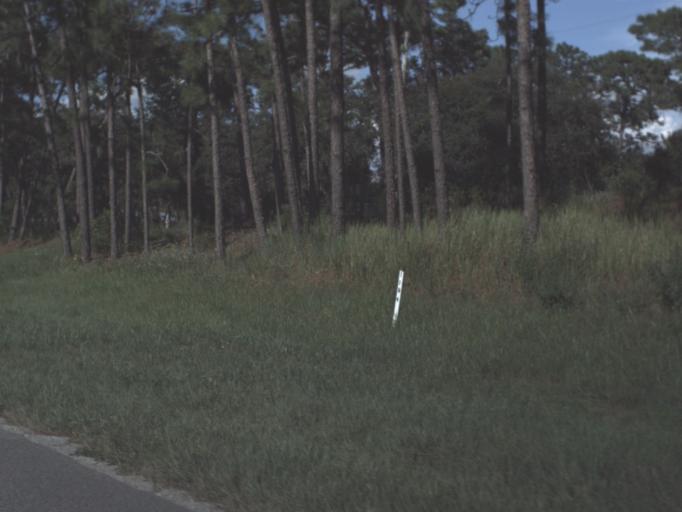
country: US
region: Florida
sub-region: Polk County
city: Polk City
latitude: 28.2733
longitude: -81.8287
